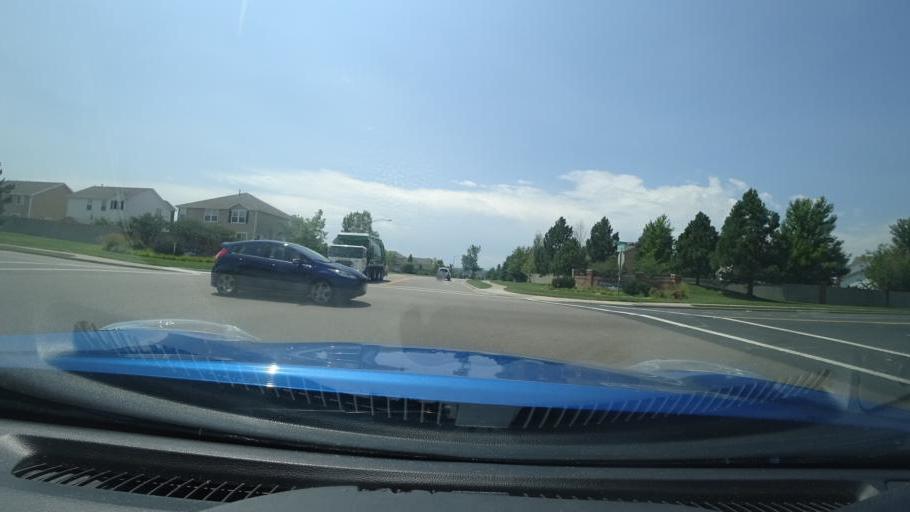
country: US
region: Colorado
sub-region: Adams County
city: Aurora
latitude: 39.6753
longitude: -104.7625
